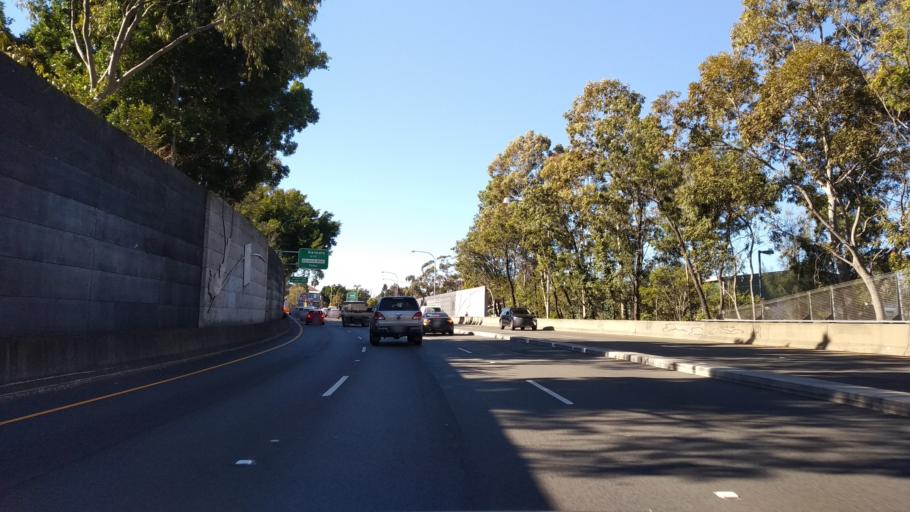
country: AU
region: New South Wales
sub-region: Leichhardt
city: Leichhardt
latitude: -33.8749
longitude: 151.1526
